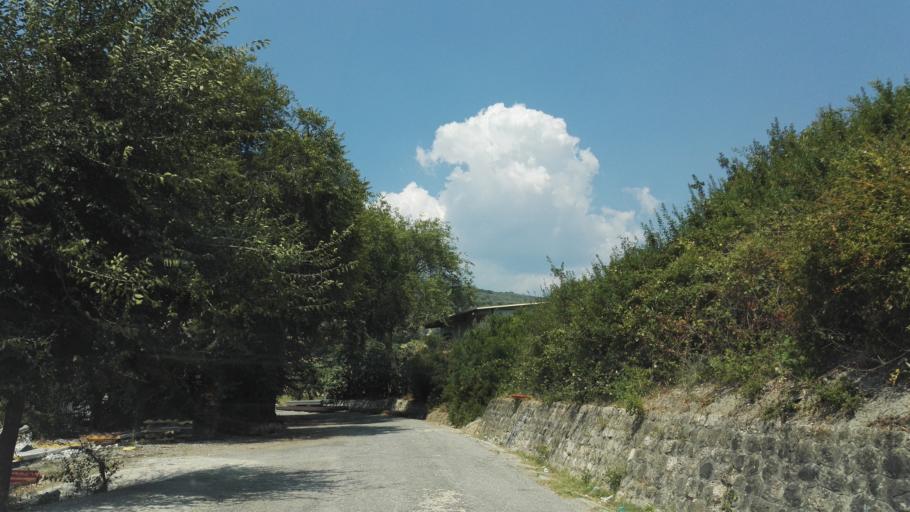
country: IT
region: Calabria
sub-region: Provincia di Reggio Calabria
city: Stilo
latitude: 38.4652
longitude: 16.4988
